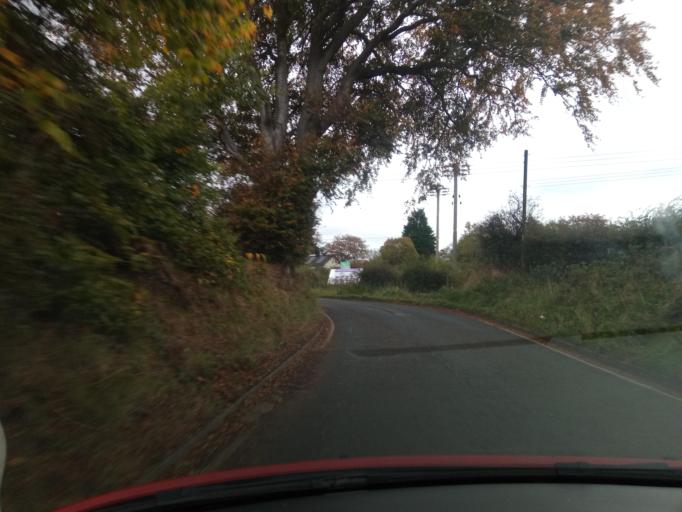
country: GB
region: Scotland
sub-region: West Lothian
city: Bathgate
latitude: 55.9157
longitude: -3.6380
